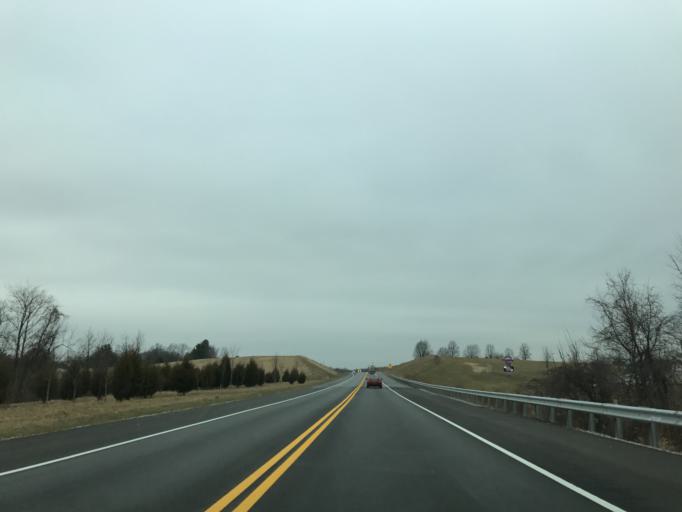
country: US
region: Maryland
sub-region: Carroll County
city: Westminster
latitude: 39.6044
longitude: -77.0566
